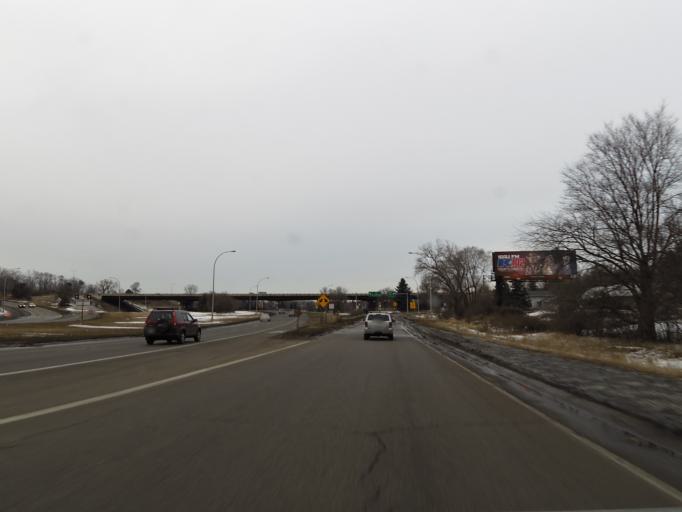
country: US
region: Minnesota
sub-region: Ramsey County
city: Maplewood
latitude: 44.9502
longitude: -93.0405
